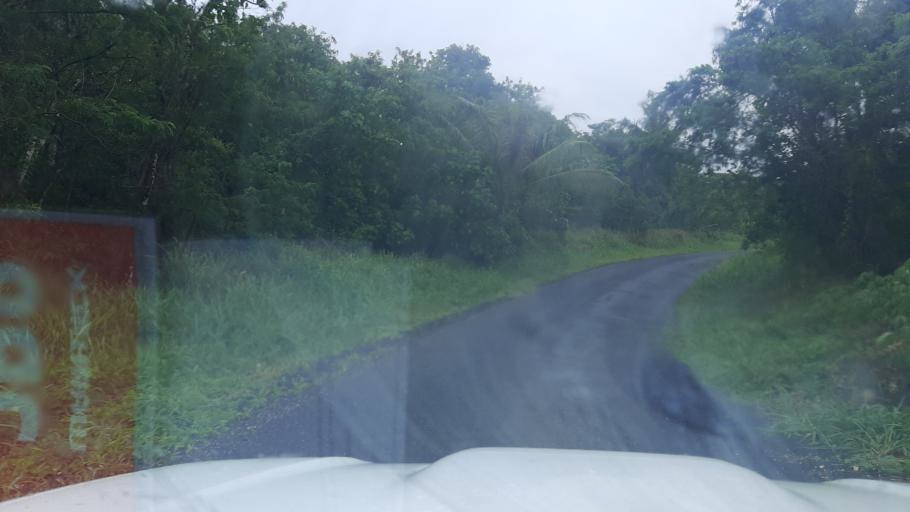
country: VU
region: Shefa
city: Port-Vila
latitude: -17.6389
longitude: 168.2115
